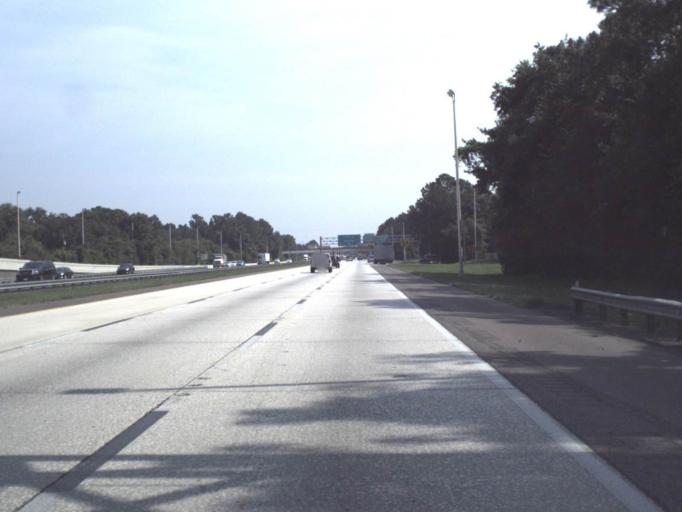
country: US
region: Florida
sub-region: Duval County
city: Jacksonville
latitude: 30.4634
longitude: -81.6482
